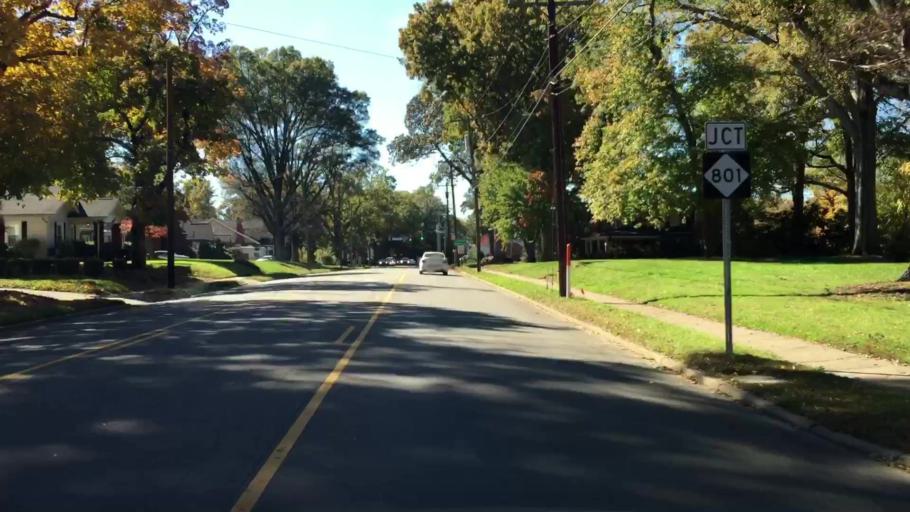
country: US
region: North Carolina
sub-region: Iredell County
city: Mooresville
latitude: 35.5881
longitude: -80.7976
